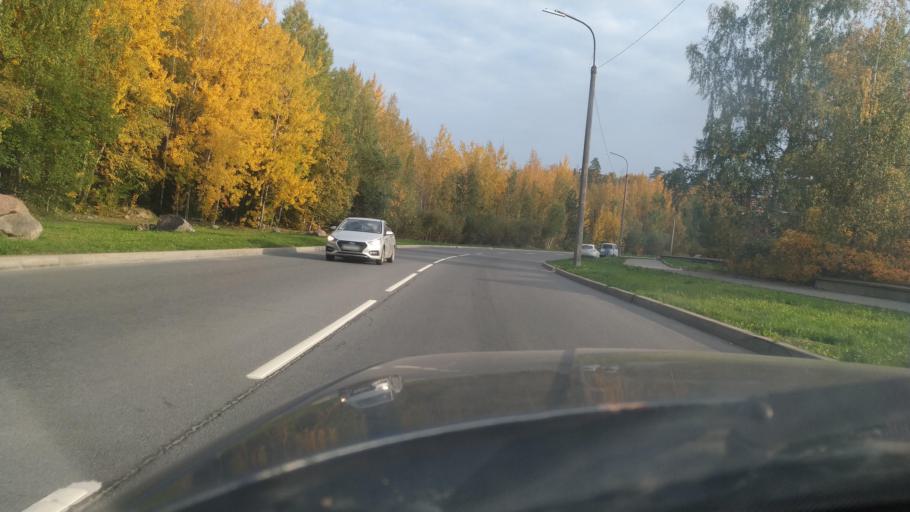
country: RU
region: Leningrad
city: Sosnovyy Bor
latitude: 59.9127
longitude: 29.0779
